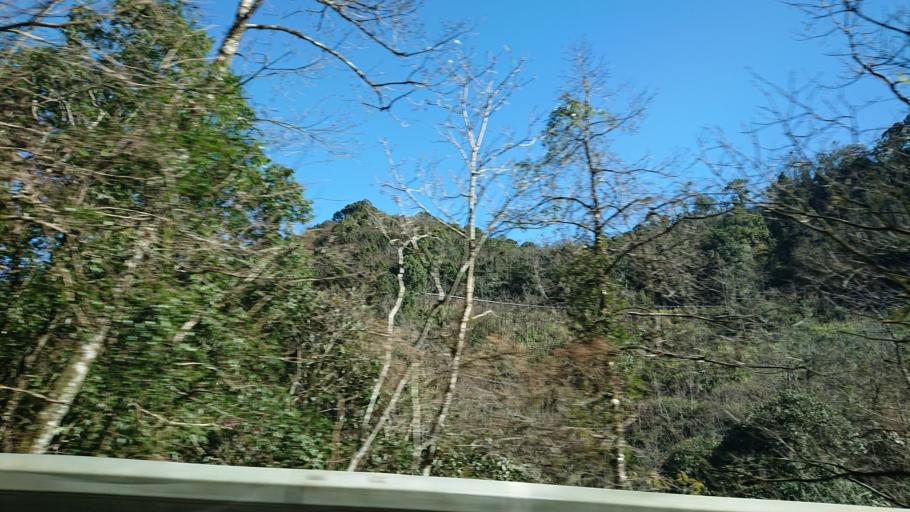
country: TW
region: Taiwan
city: Daxi
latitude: 24.4036
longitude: 121.3656
